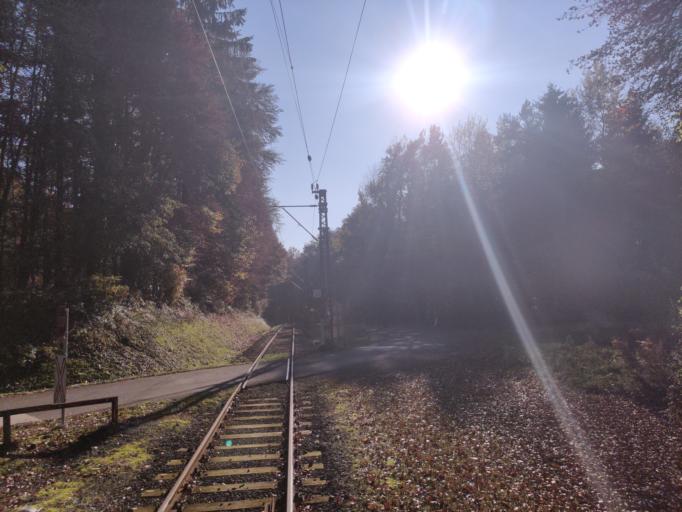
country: AT
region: Styria
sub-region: Politischer Bezirk Suedoststeiermark
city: Gnas
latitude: 46.8836
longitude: 15.8309
